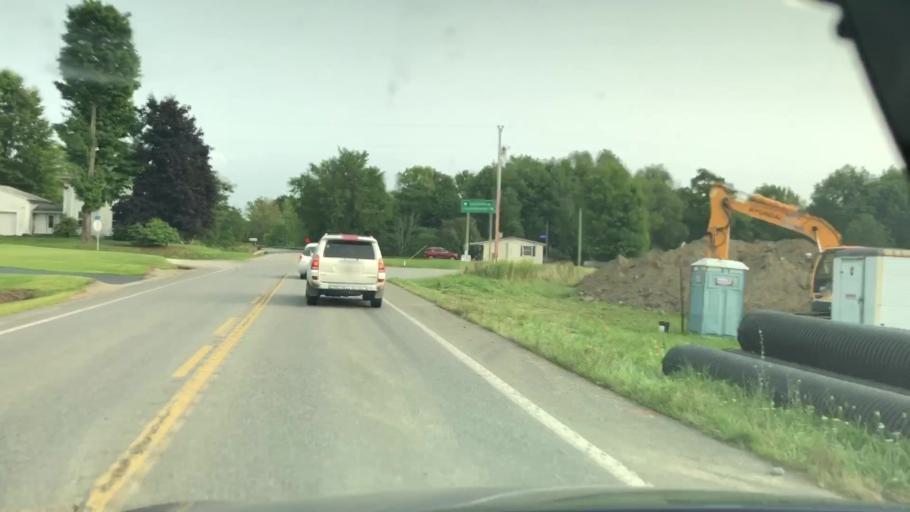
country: US
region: Pennsylvania
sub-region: Erie County
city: Union City
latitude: 41.8203
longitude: -79.8083
